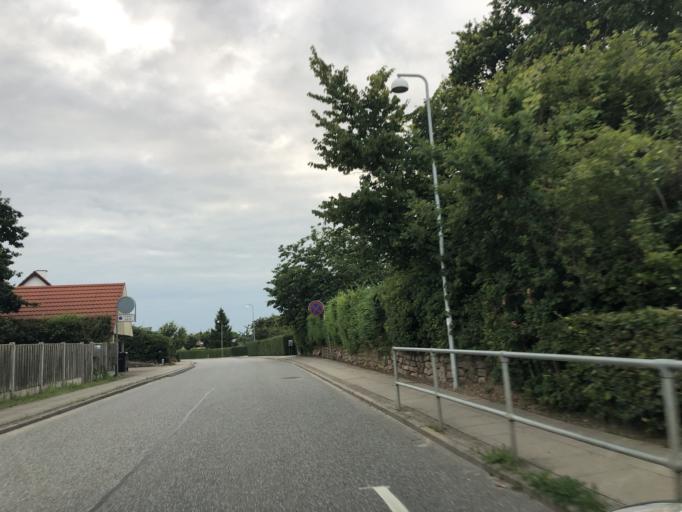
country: DK
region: South Denmark
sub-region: Vejle Kommune
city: Vejle
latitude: 55.6906
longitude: 9.5533
